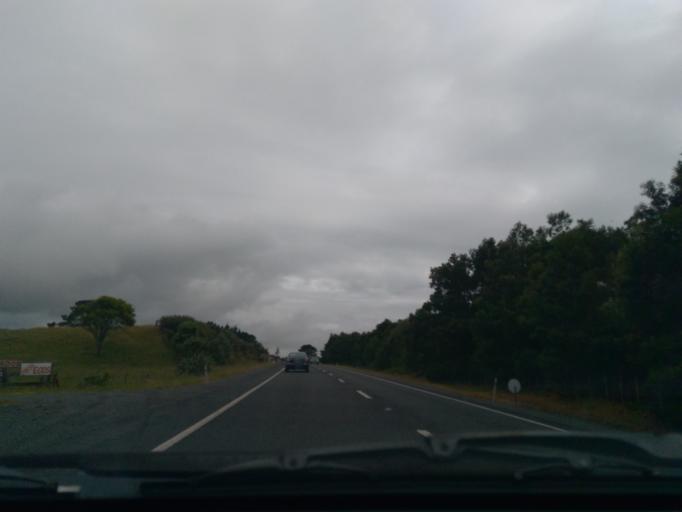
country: NZ
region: Northland
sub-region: Whangarei
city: Ruakaka
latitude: -35.9389
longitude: 174.4560
